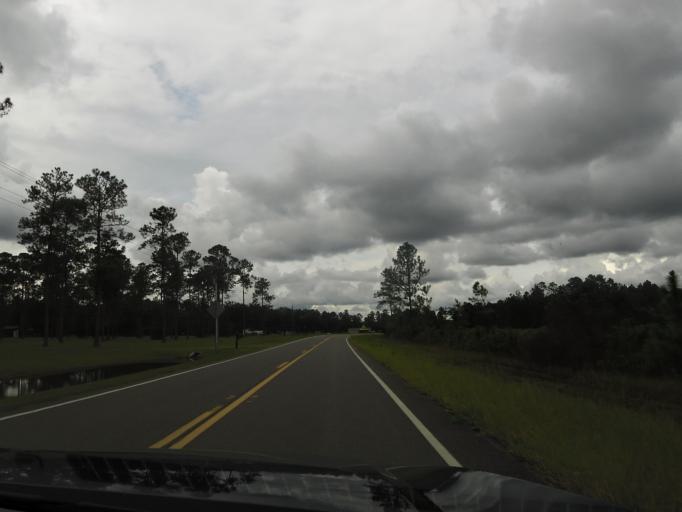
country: US
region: Florida
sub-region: Baker County
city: Macclenny
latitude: 30.4668
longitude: -82.1990
